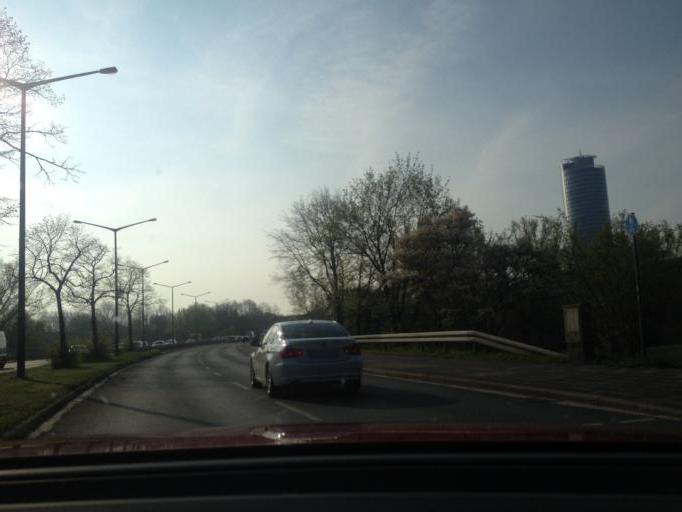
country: DE
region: Bavaria
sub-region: Regierungsbezirk Mittelfranken
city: Nuernberg
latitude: 49.4595
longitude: 11.1141
